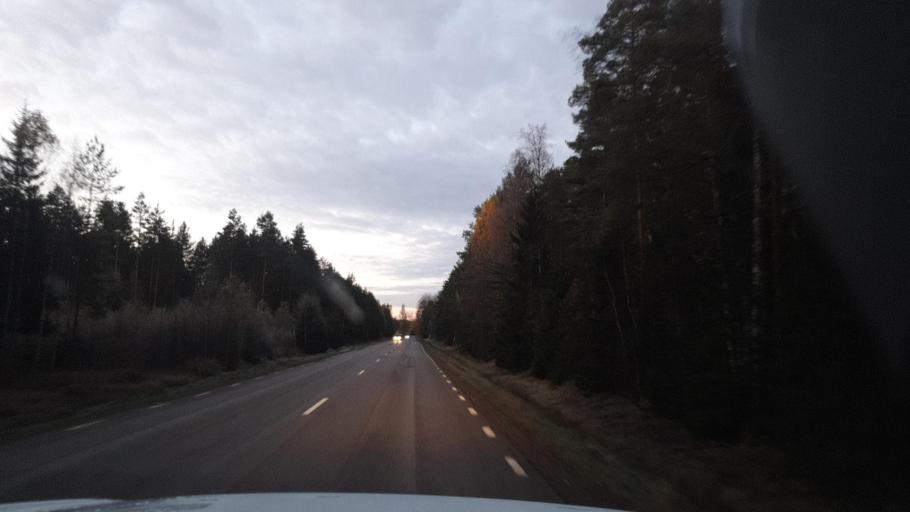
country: SE
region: Vaermland
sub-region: Eda Kommun
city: Charlottenberg
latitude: 59.8238
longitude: 12.2622
